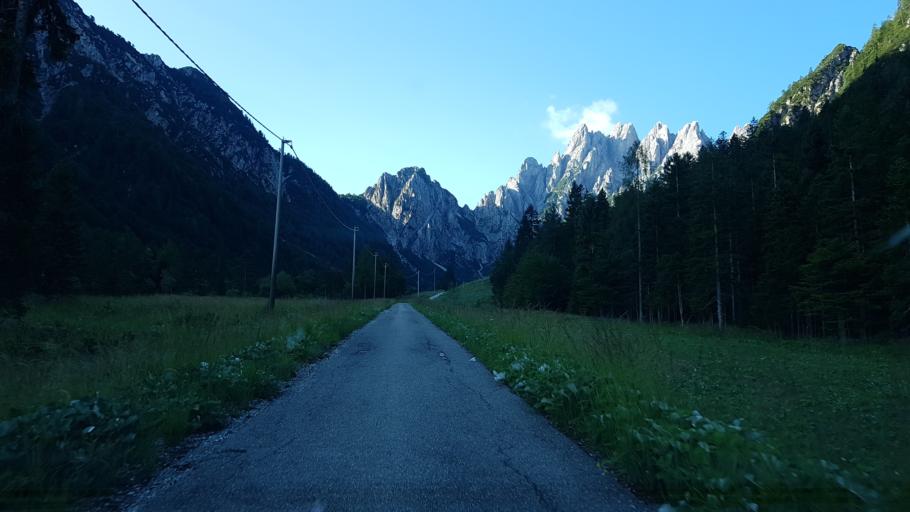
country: IT
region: Friuli Venezia Giulia
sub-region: Provincia di Udine
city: Pontebba
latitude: 46.4970
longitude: 13.2537
